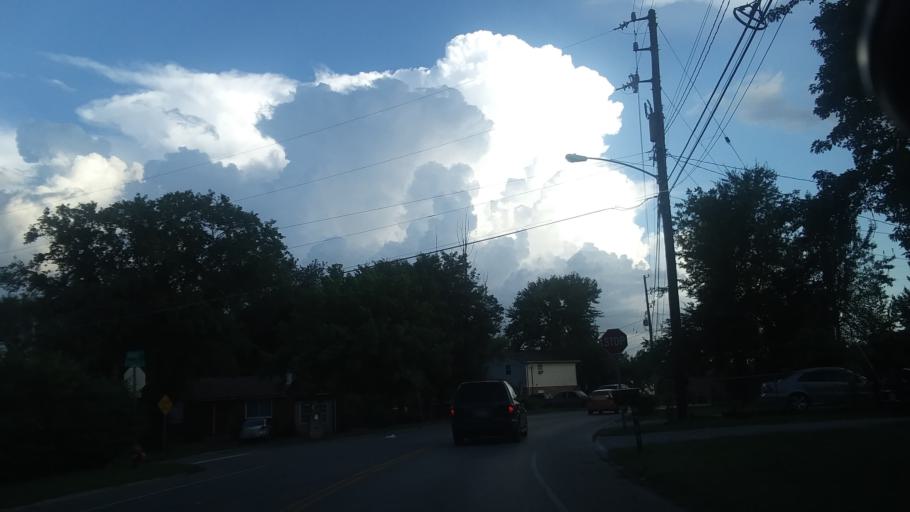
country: US
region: Tennessee
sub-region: Rutherford County
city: La Vergne
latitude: 36.0697
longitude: -86.6666
